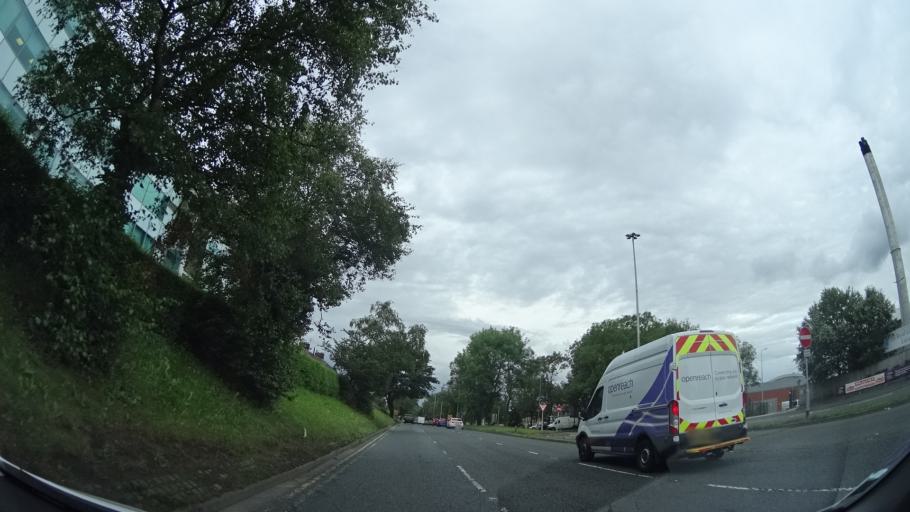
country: GB
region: England
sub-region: Knowsley
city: Huyton
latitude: 53.4111
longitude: -2.9024
